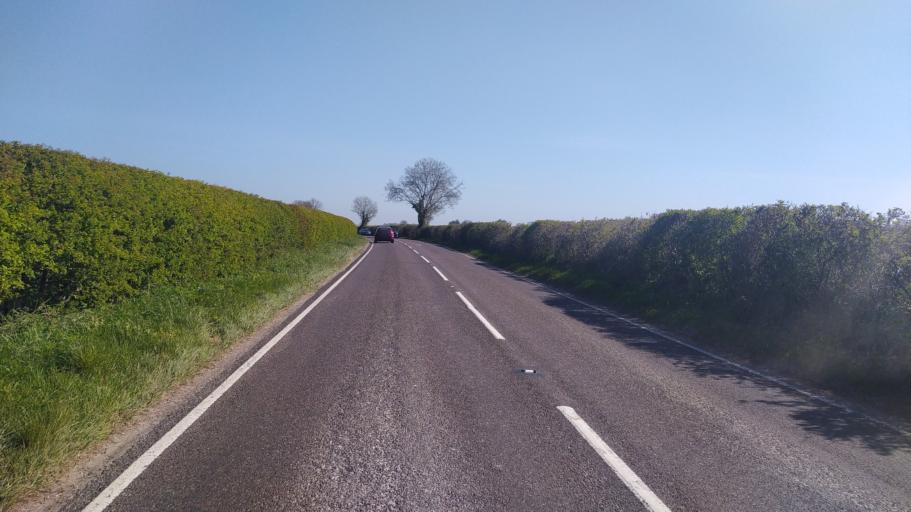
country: GB
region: England
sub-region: Dorset
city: Wimborne Minster
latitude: 50.8591
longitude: -1.9940
